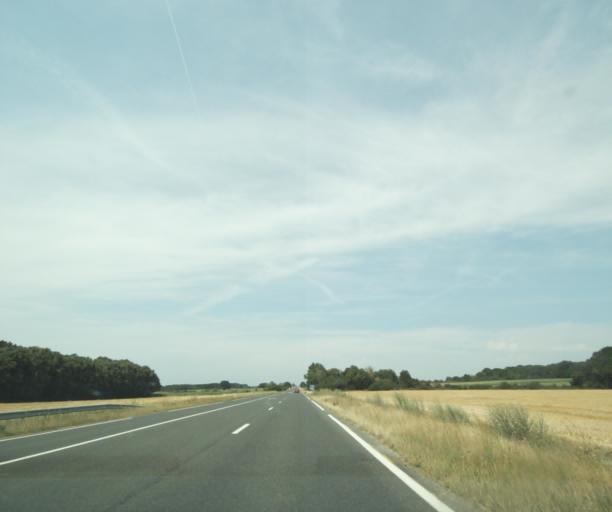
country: FR
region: Centre
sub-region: Departement d'Indre-et-Loire
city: Sorigny
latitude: 47.1830
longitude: 0.6608
